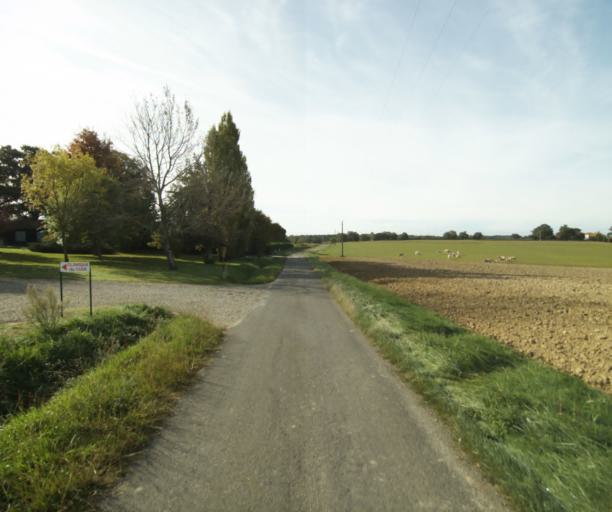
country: FR
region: Midi-Pyrenees
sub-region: Departement du Gers
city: Eauze
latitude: 43.9156
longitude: 0.1204
